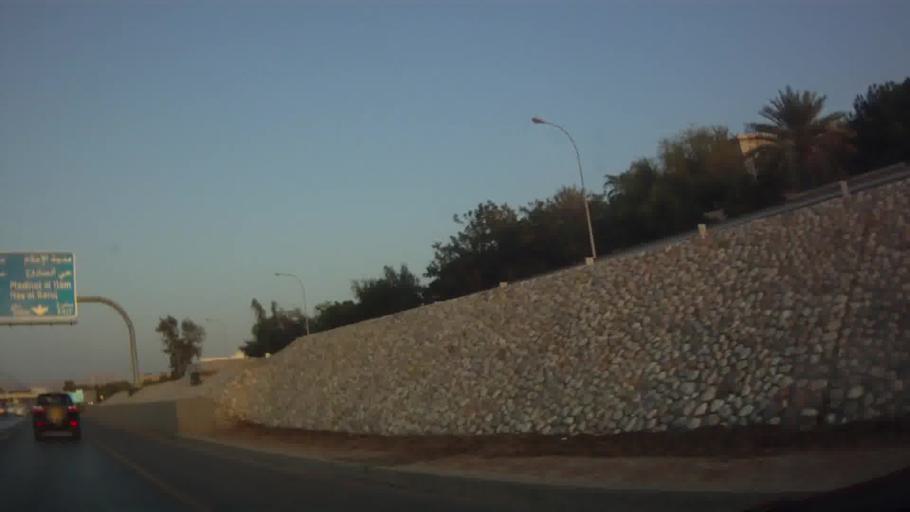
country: OM
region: Muhafazat Masqat
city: Bawshar
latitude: 23.6125
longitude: 58.4685
